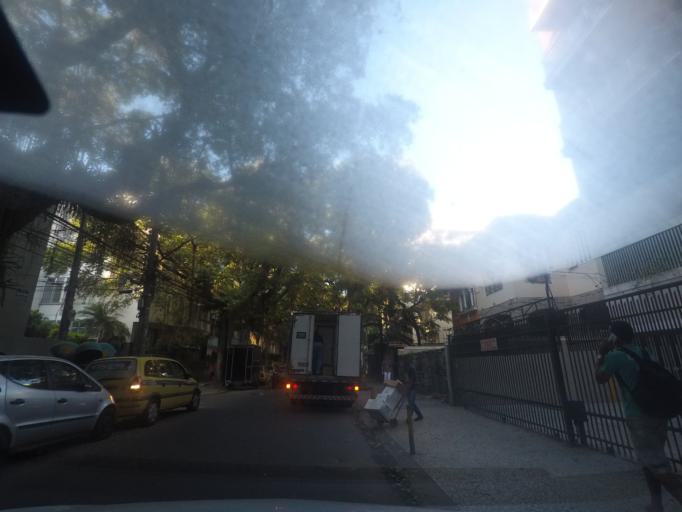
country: BR
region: Rio de Janeiro
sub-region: Rio De Janeiro
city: Rio de Janeiro
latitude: -22.9577
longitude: -43.1841
